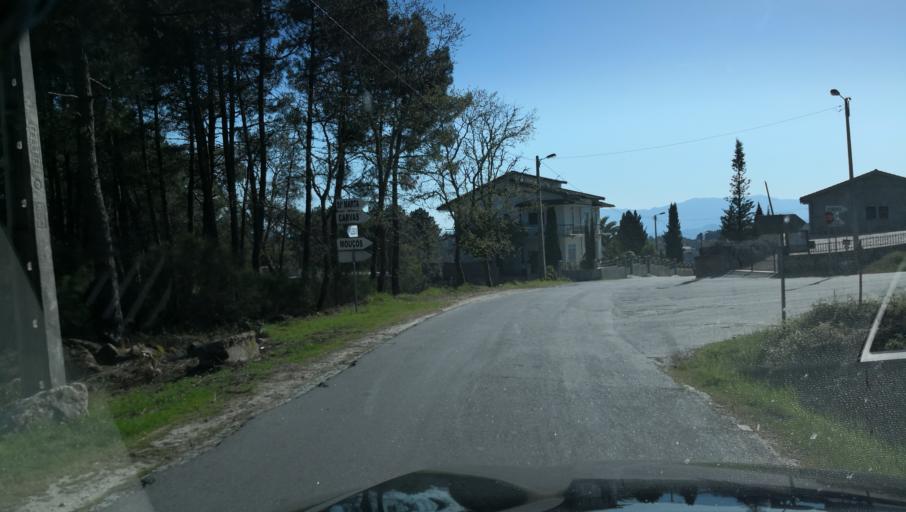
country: PT
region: Vila Real
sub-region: Vila Real
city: Vila Real
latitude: 41.2919
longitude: -7.6715
